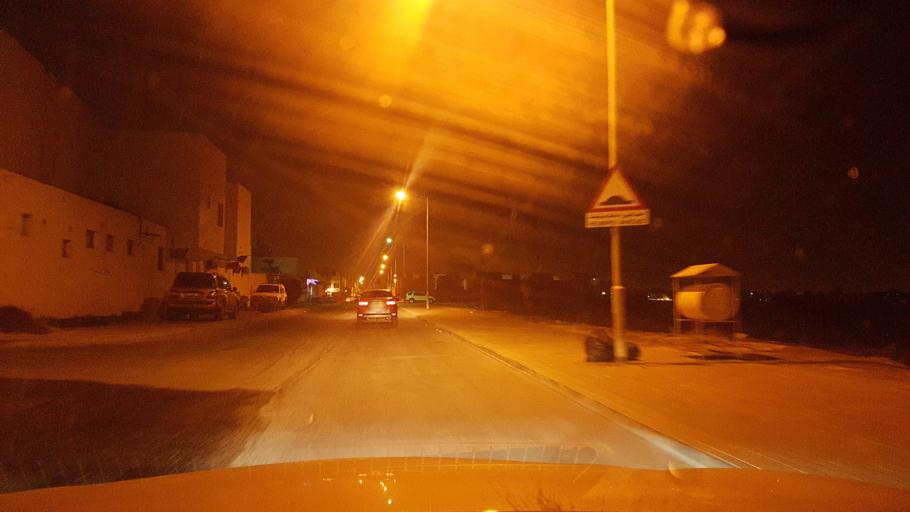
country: BH
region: Central Governorate
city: Madinat Hamad
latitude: 26.0942
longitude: 50.4800
